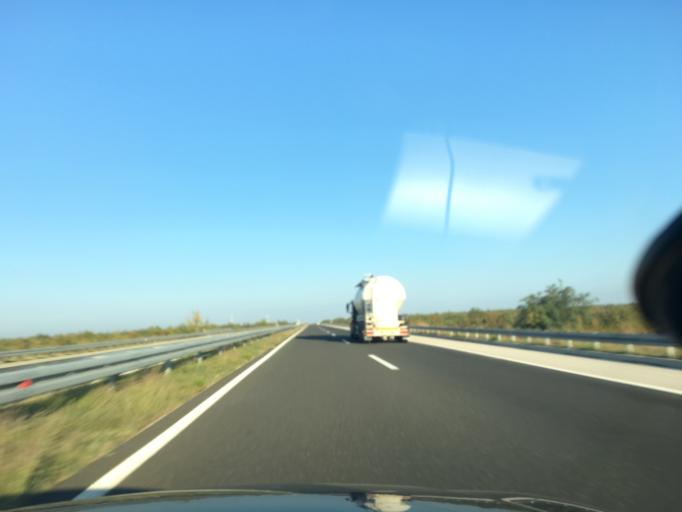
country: HR
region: Zadarska
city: Benkovac
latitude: 43.9966
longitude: 15.6121
